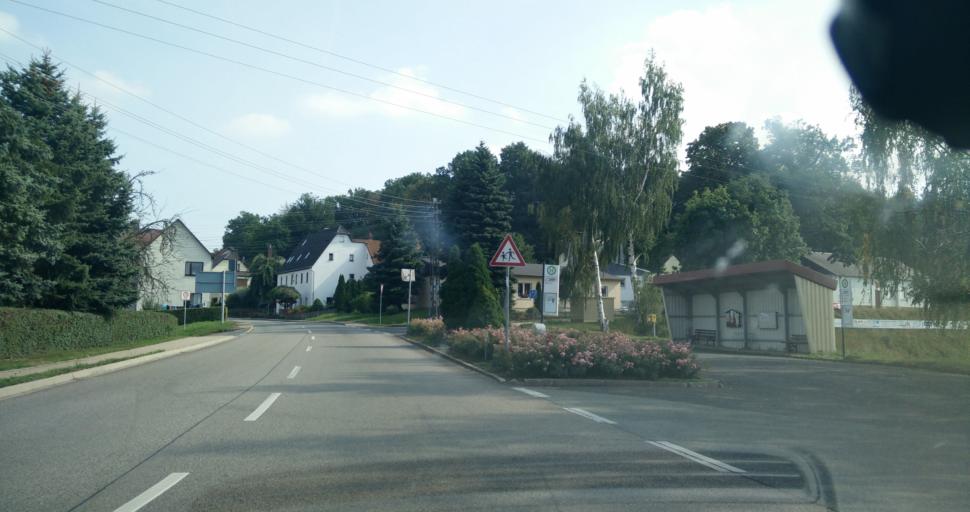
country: DE
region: Saxony
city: Konigsfeld
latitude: 51.0597
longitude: 12.7561
